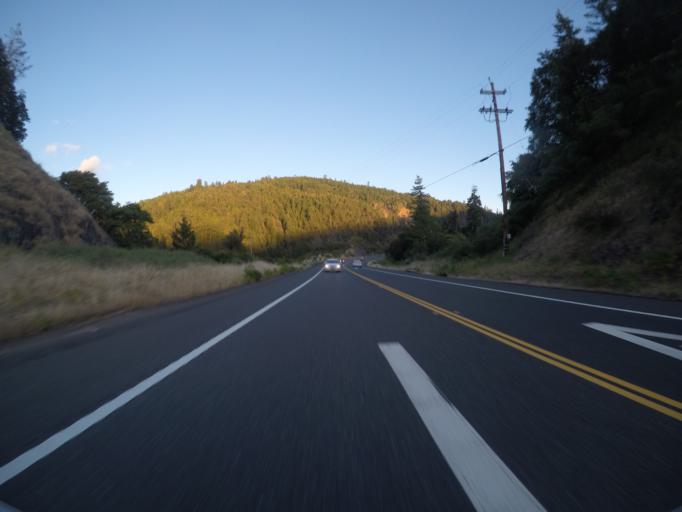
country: US
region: California
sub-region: Humboldt County
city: Redway
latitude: 39.9298
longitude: -123.7625
